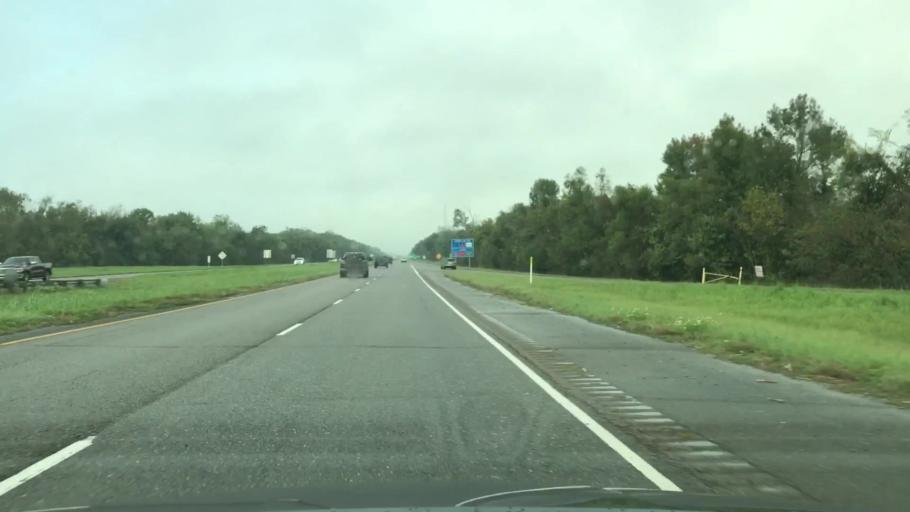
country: US
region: Louisiana
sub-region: Terrebonne Parish
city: Gray
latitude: 29.6824
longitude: -90.7546
